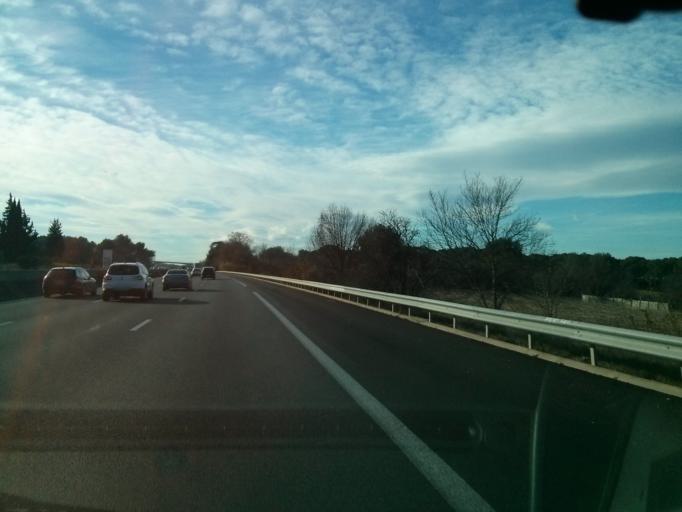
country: FR
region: Languedoc-Roussillon
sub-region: Departement de l'Herault
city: Lunel-Viel
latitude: 43.6960
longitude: 4.0885
